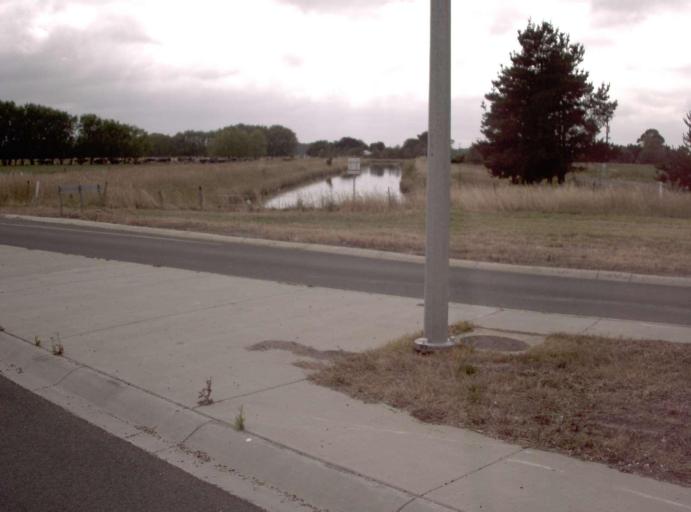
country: AU
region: Victoria
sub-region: Wellington
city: Heyfield
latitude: -38.0216
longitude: 146.7656
